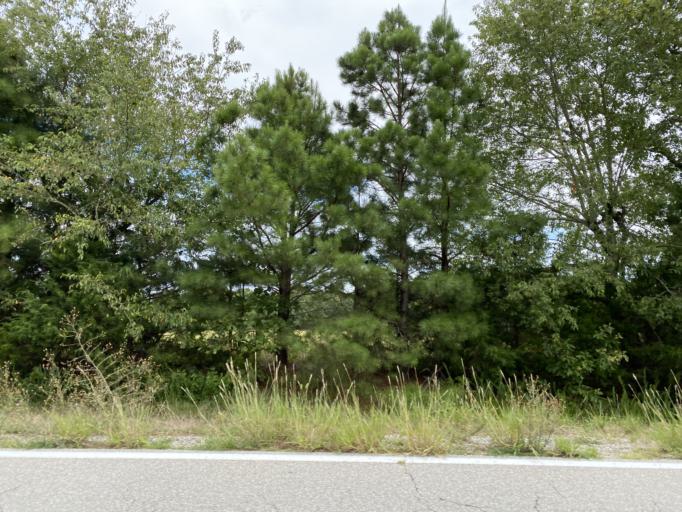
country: US
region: Arkansas
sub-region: Fulton County
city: Salem
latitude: 36.4259
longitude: -91.7077
